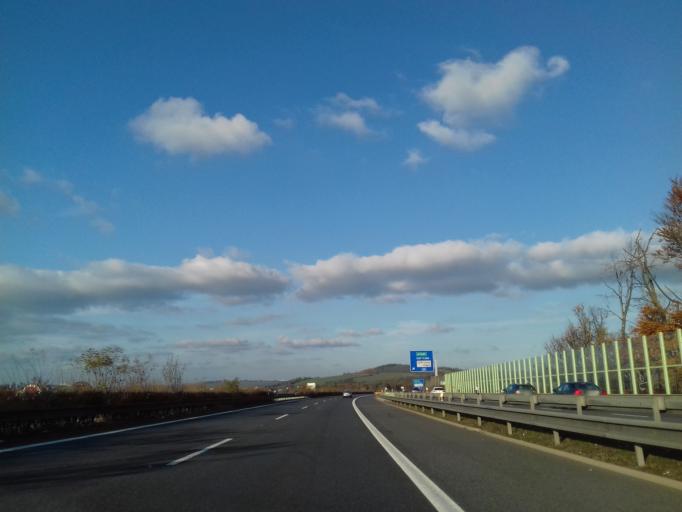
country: CZ
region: Plzensky
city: Stenovice
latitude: 49.6972
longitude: 13.4310
